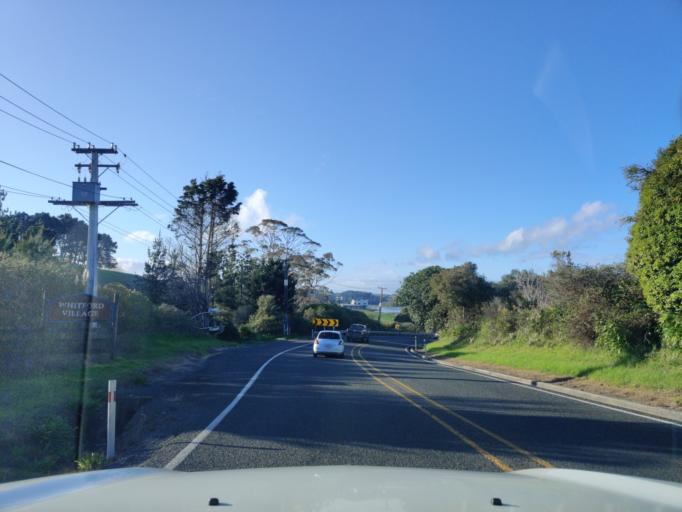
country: NZ
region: Auckland
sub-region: Auckland
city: Pakuranga
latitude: -36.9440
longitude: 174.9608
